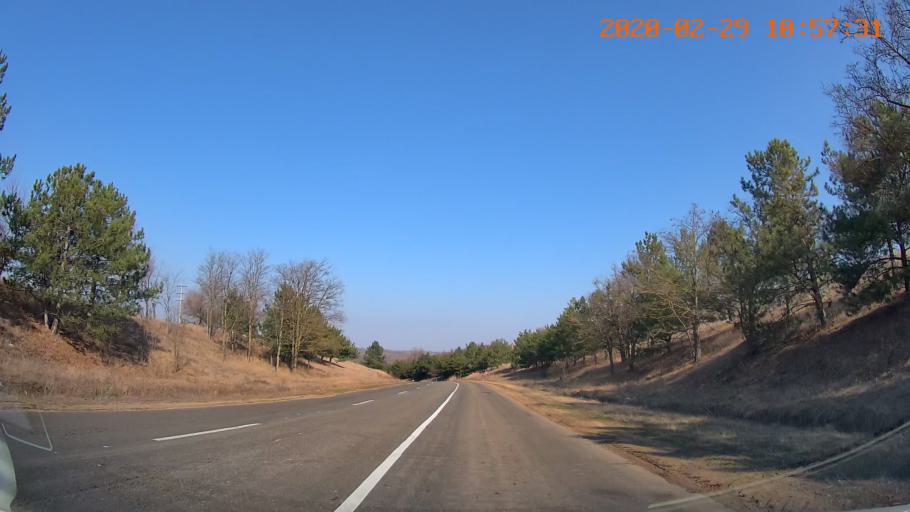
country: MD
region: Telenesti
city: Grigoriopol
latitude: 47.1603
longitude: 29.3219
